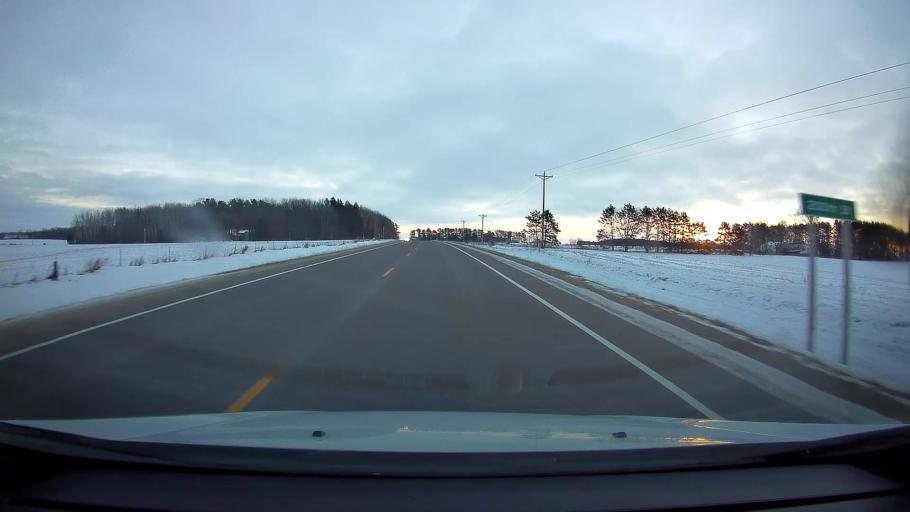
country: US
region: Wisconsin
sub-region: Saint Croix County
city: New Richmond
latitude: 45.1368
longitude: -92.4082
